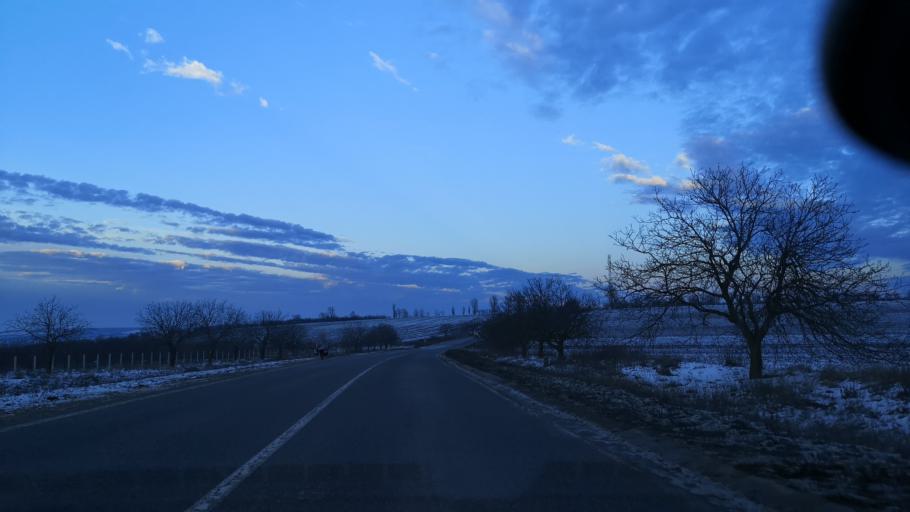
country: MD
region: Orhei
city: Orhei
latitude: 47.5784
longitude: 28.8036
